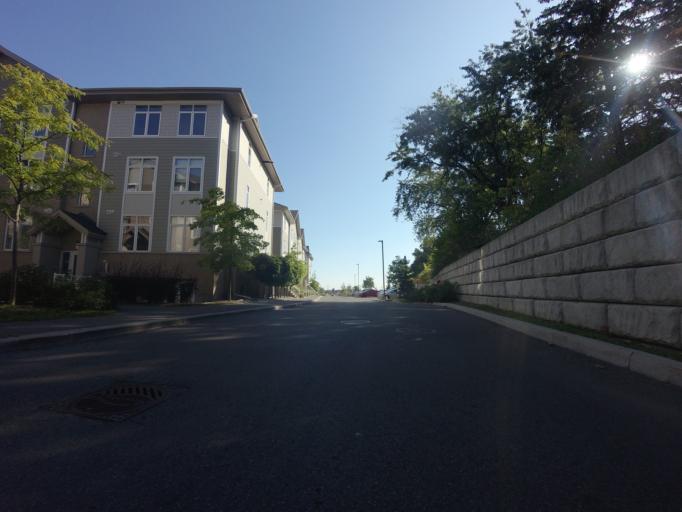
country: CA
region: Ontario
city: Ottawa
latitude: 45.4041
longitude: -75.6310
